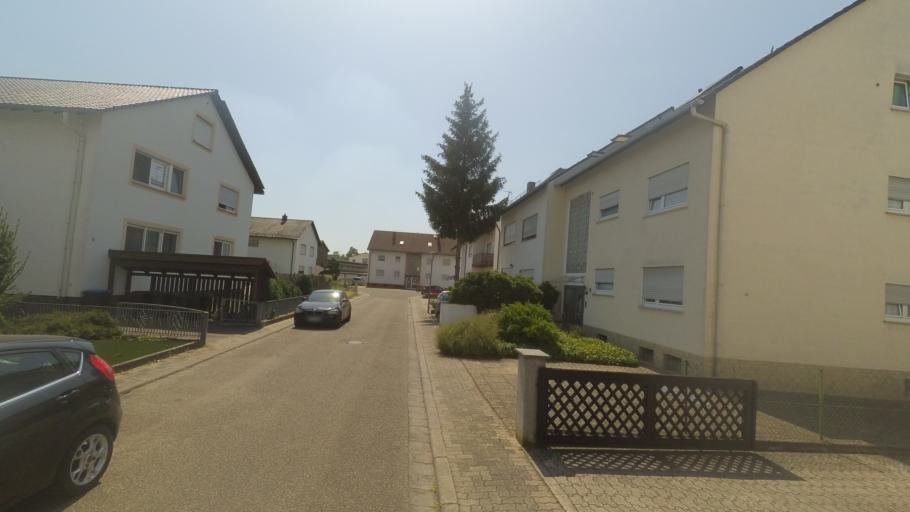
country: DE
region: Rheinland-Pfalz
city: Schifferstadt
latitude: 49.3952
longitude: 8.3679
